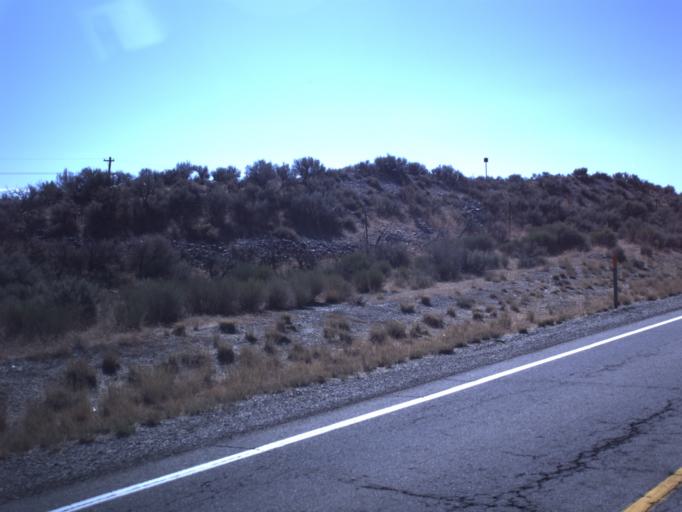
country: US
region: Utah
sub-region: Tooele County
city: Tooele
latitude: 40.3524
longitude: -112.4125
